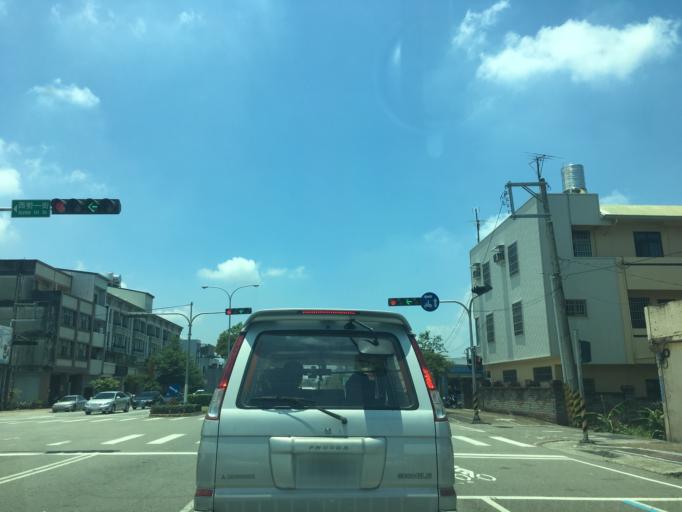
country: TW
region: Taiwan
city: Fengyuan
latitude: 24.2448
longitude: 120.7031
